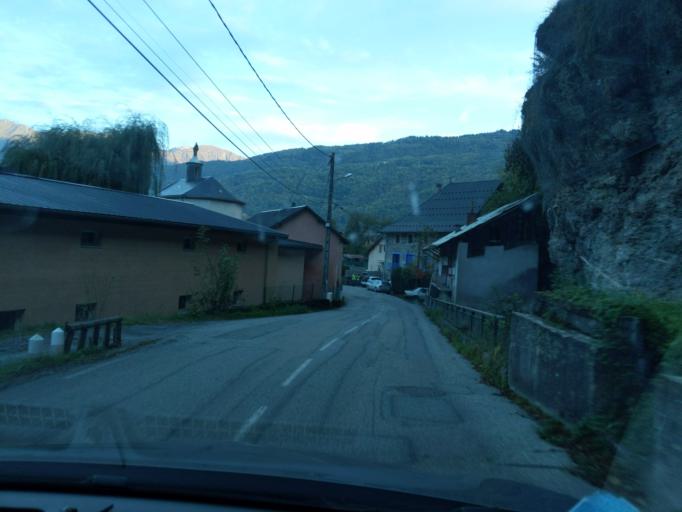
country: FR
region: Rhone-Alpes
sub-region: Departement de la Savoie
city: Aiton
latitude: 45.5403
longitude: 6.3081
